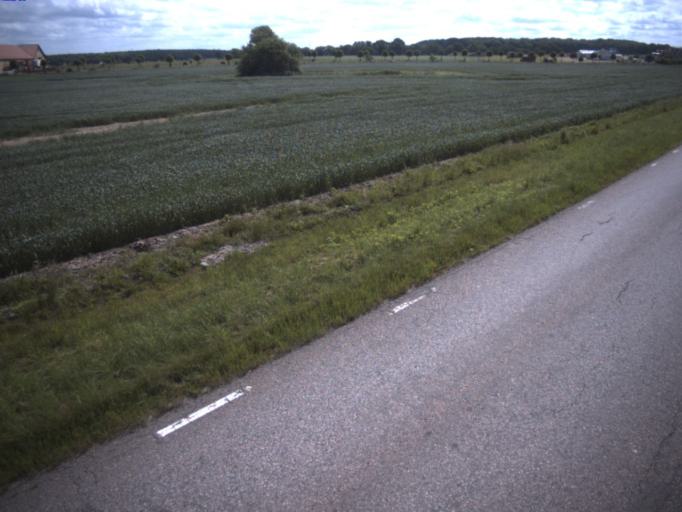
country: SE
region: Skane
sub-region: Helsingborg
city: Odakra
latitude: 56.0862
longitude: 12.7000
